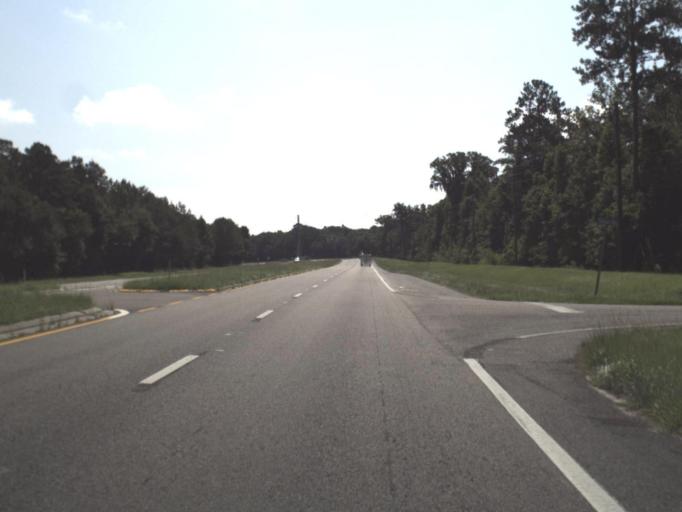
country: US
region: Florida
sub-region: Hernando County
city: Brooksville
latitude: 28.5383
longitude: -82.3811
